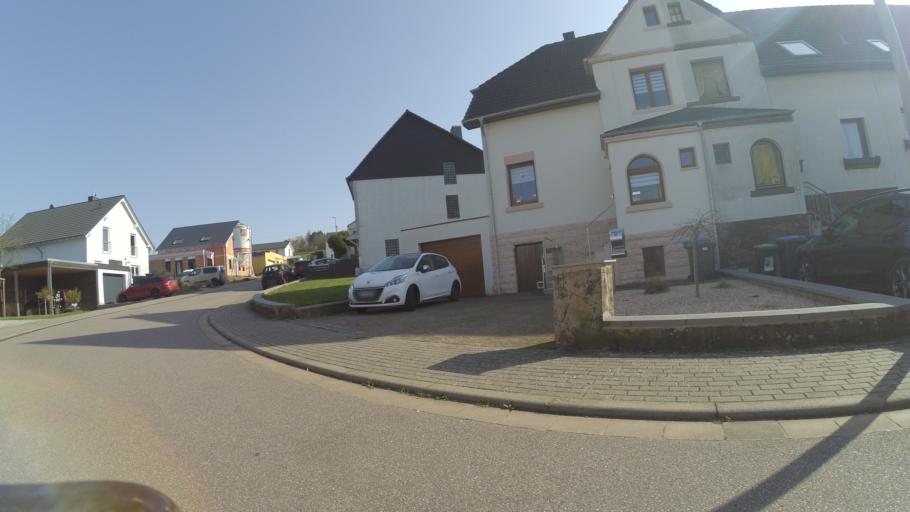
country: DE
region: Saarland
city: Heusweiler
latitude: 49.3316
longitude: 6.9454
